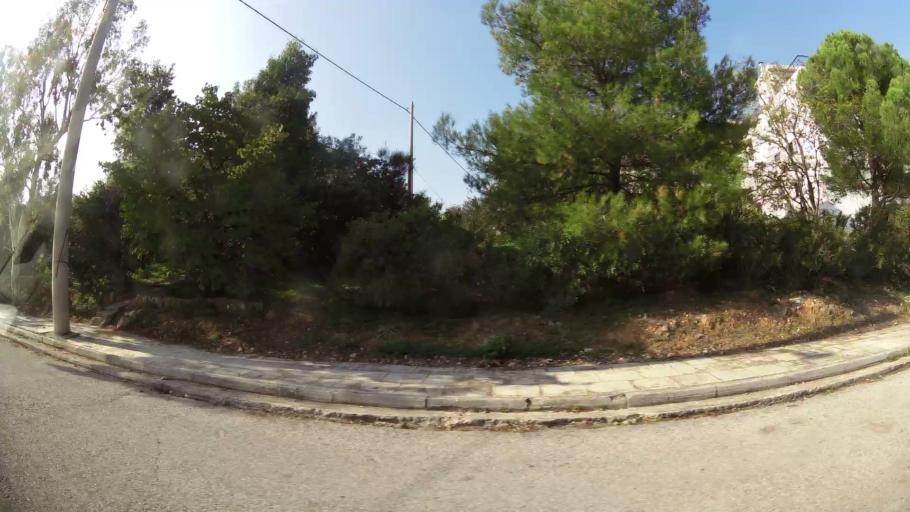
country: GR
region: Attica
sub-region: Nomarchia Athinas
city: Papagou
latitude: 37.9877
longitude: 23.8003
